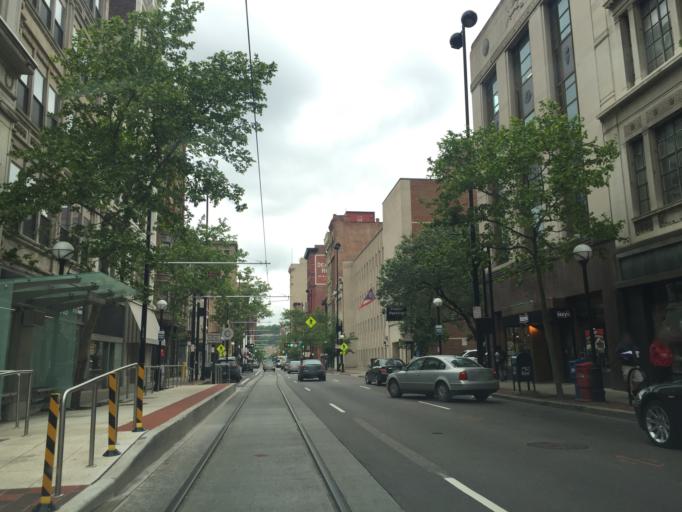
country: US
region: Kentucky
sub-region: Campbell County
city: Newport
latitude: 39.1030
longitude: -84.5101
